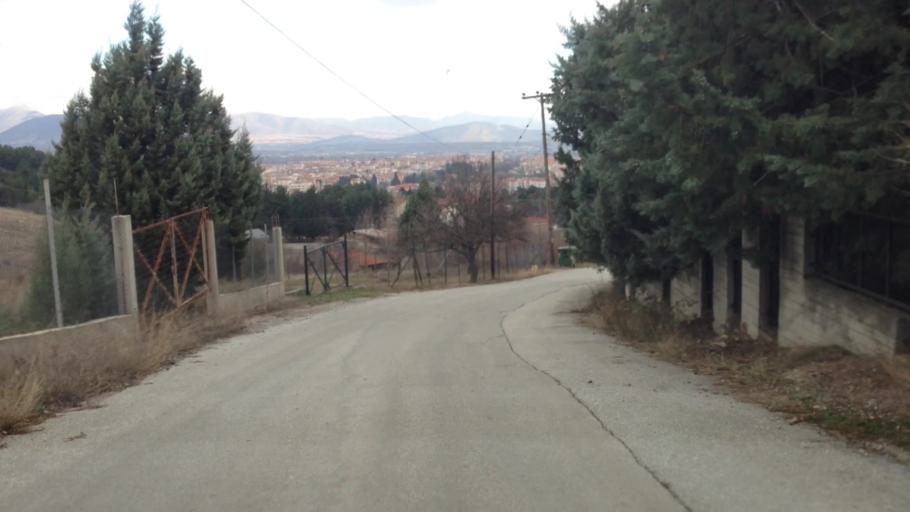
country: GR
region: West Macedonia
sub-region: Nomos Kozanis
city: Kozani
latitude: 40.2921
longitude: 21.7715
